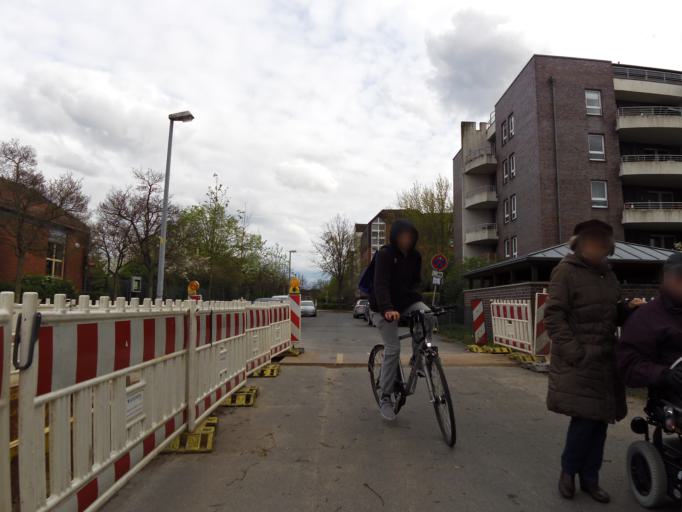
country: DE
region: Lower Saxony
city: Laatzen
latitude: 52.3863
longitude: 9.8147
